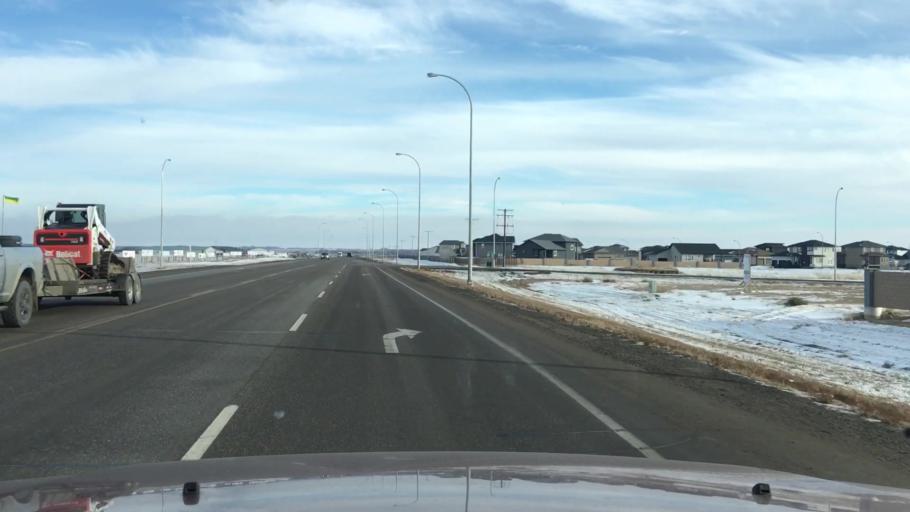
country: CA
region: Saskatchewan
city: Pilot Butte
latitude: 50.4875
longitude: -104.4220
